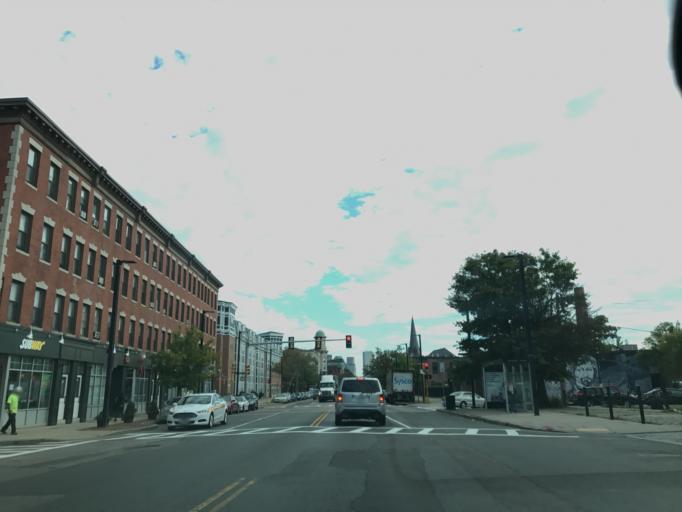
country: US
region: Massachusetts
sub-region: Suffolk County
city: Boston
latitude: 42.3370
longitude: -71.0845
